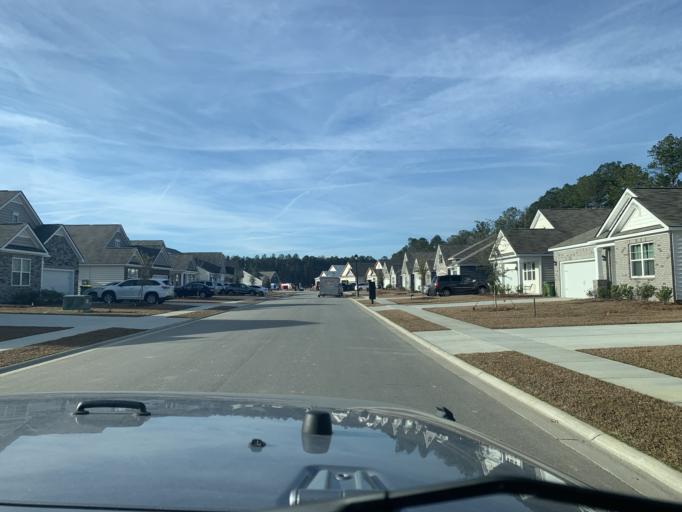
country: US
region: Georgia
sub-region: Chatham County
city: Pooler
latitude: 32.0692
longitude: -81.2579
